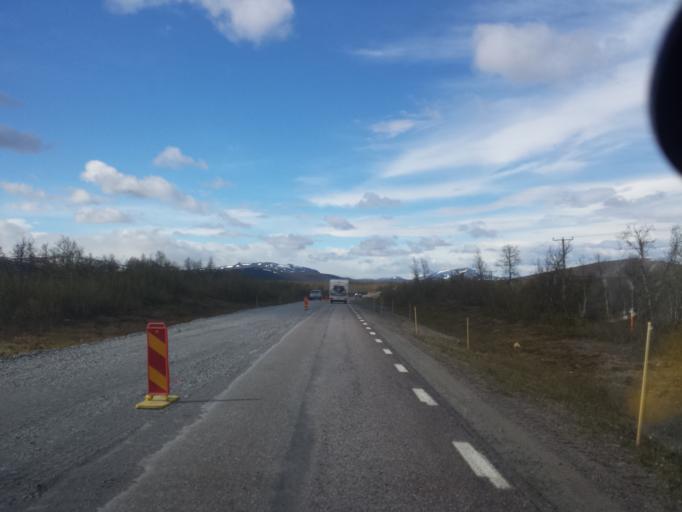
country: SE
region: Norrbotten
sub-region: Kiruna Kommun
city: Kiruna
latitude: 68.0098
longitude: 19.8453
